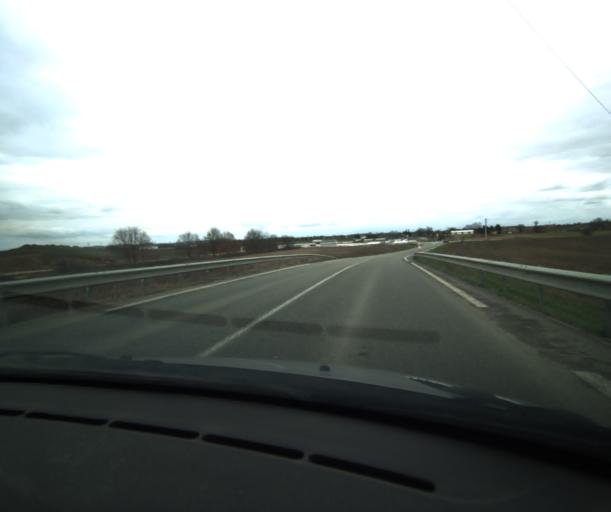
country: FR
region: Midi-Pyrenees
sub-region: Departement du Tarn-et-Garonne
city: Castelsarrasin
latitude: 44.0645
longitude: 1.1058
